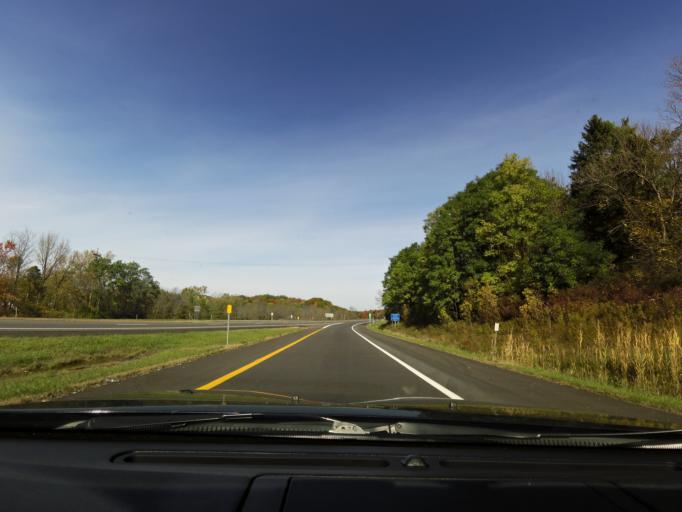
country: US
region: New York
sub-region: Erie County
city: East Aurora
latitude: 42.7692
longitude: -78.5924
